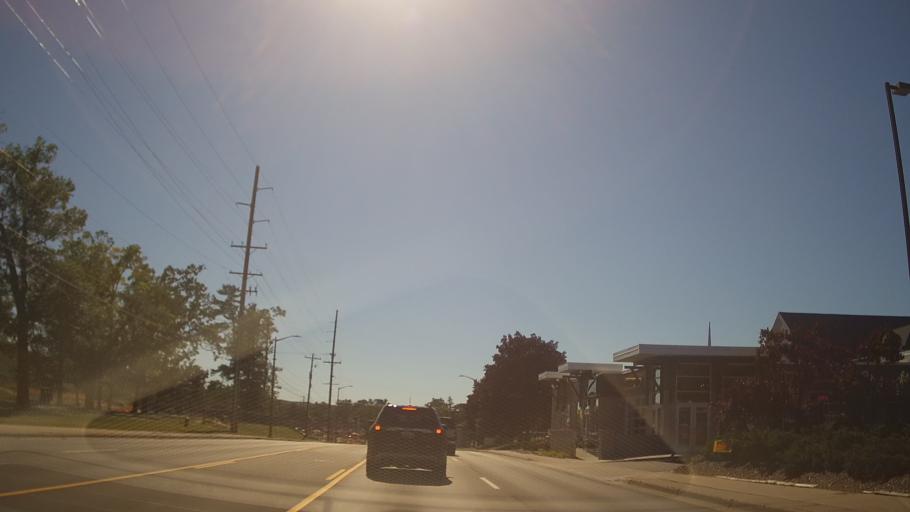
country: US
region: Michigan
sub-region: Grand Traverse County
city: Traverse City
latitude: 44.7642
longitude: -85.5919
